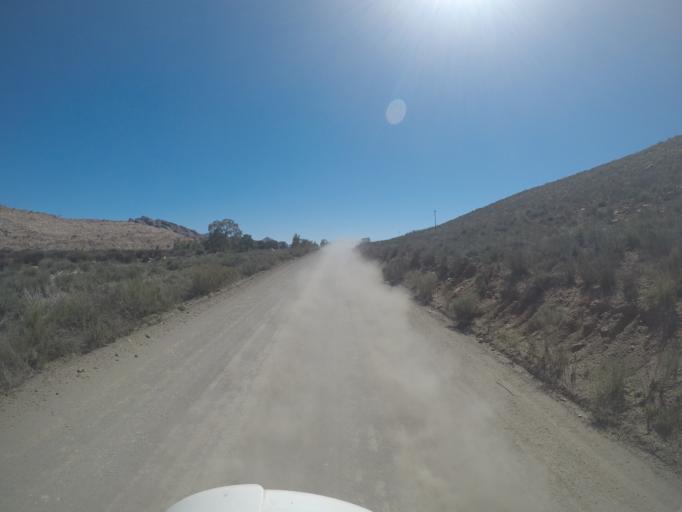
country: ZA
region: Western Cape
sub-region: Cape Winelands District Municipality
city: Ceres
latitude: -32.8174
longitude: 19.4520
